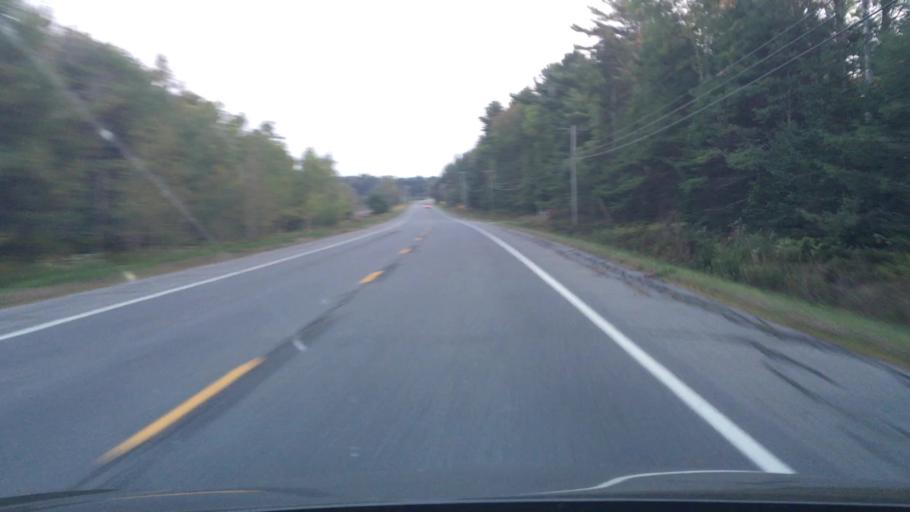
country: US
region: Maine
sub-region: Waldo County
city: Stockton Springs
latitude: 44.5441
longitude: -68.8635
